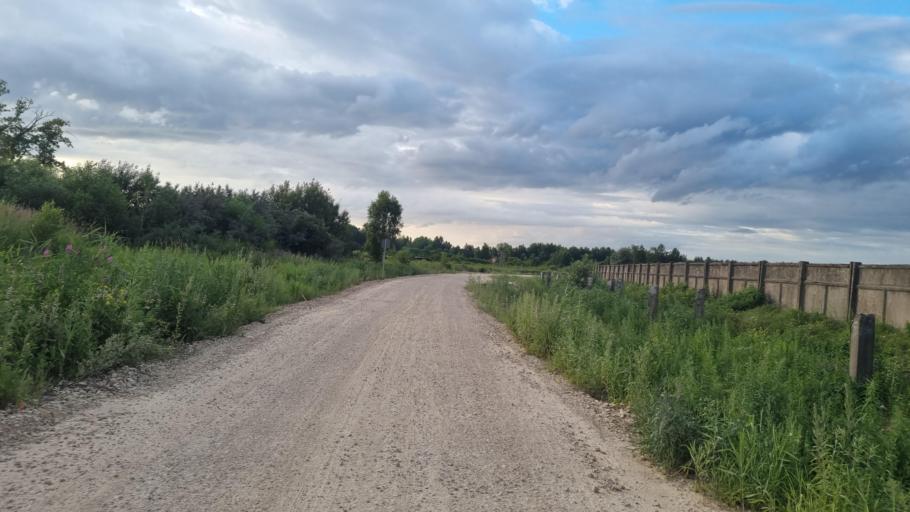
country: LV
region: Stopini
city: Ulbroka
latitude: 56.9151
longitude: 24.2390
